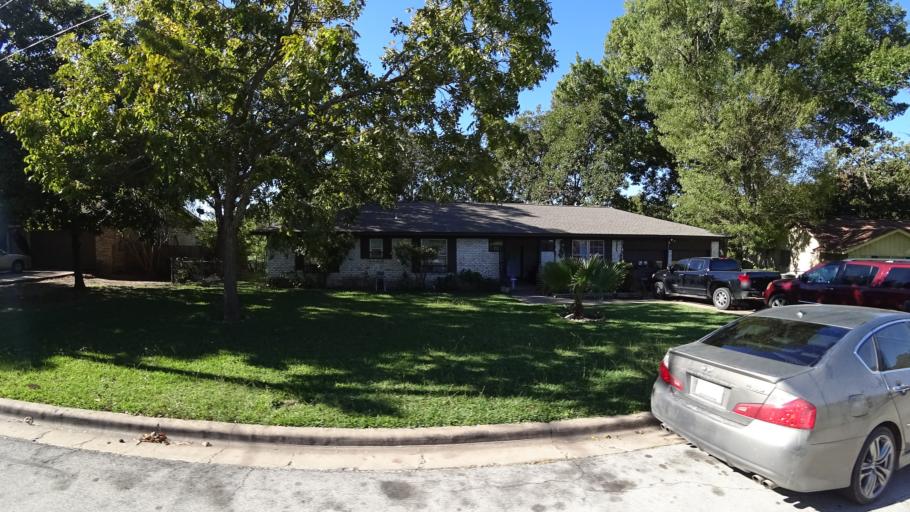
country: US
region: Texas
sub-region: Travis County
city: Manor
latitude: 30.3339
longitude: -97.6538
